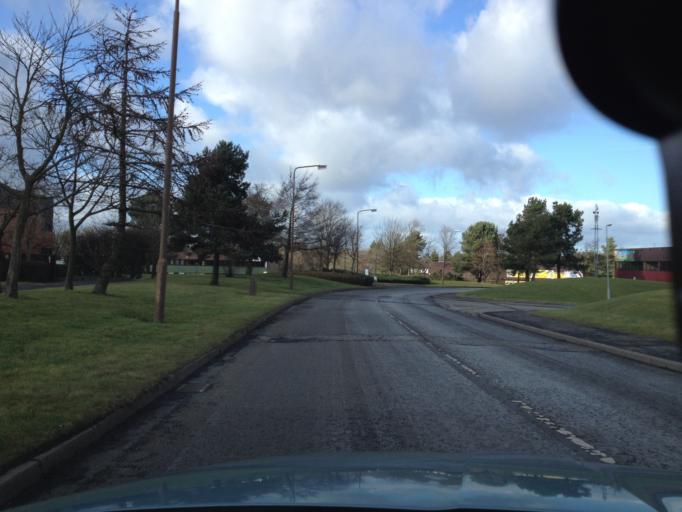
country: GB
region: Scotland
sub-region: West Lothian
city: West Calder
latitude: 55.8640
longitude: -3.5333
